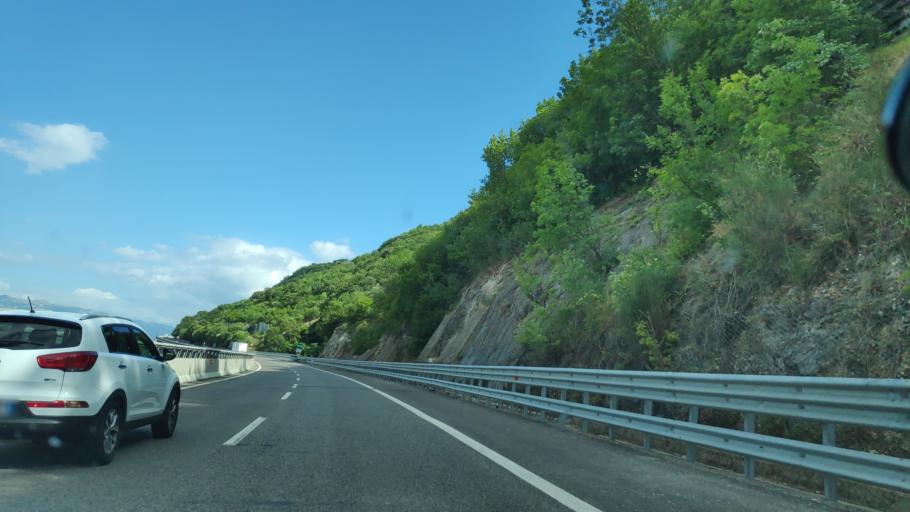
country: IT
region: Campania
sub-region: Provincia di Salerno
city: Sicignano degli Alburni
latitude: 40.5931
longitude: 15.3245
